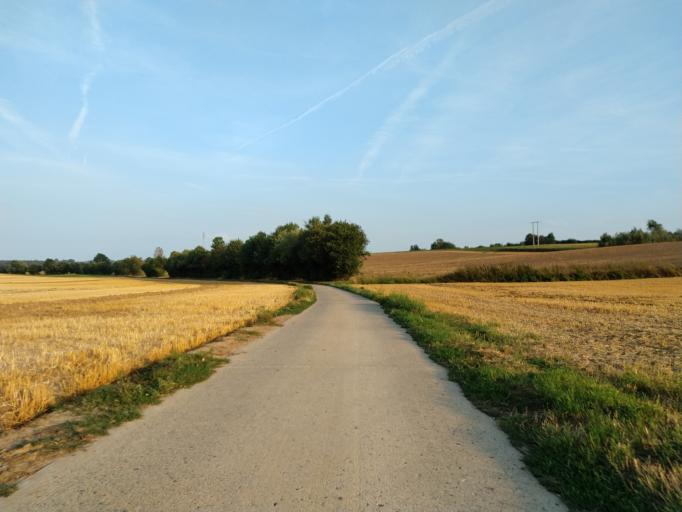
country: BE
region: Flanders
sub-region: Provincie Vlaams-Brabant
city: Hoegaarden
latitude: 50.7861
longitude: 4.8821
